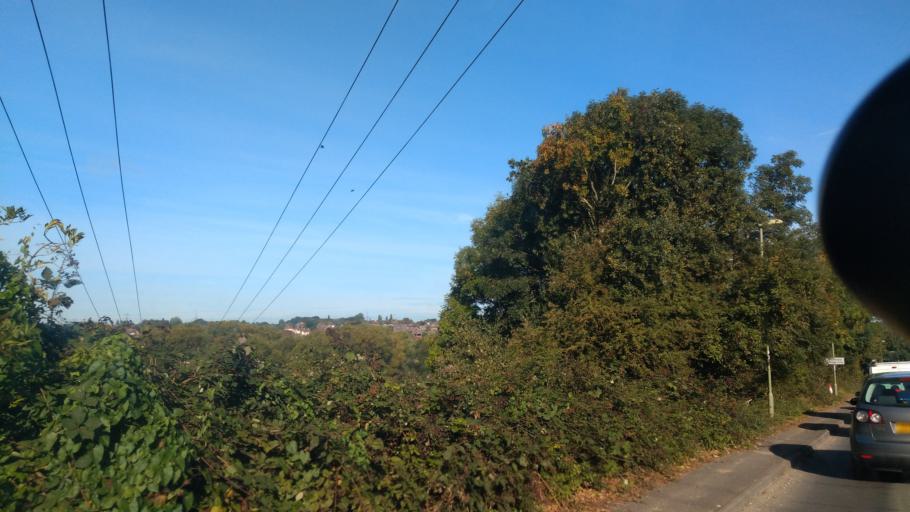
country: GB
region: England
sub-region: Hampshire
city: Fareham
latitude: 50.8447
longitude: -1.2280
